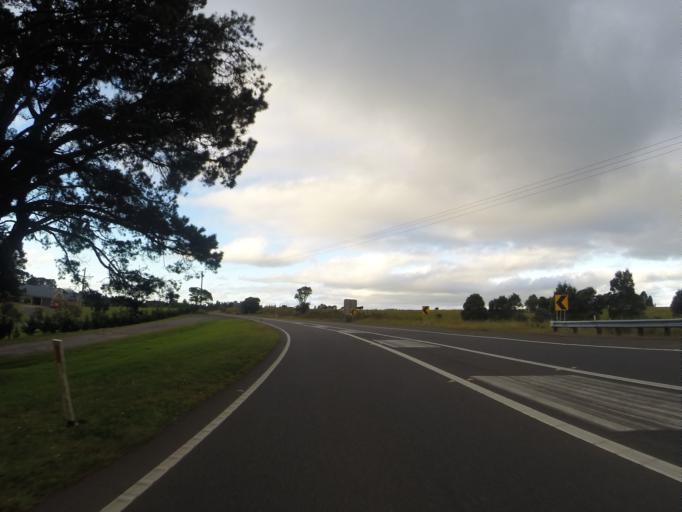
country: AU
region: New South Wales
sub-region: Shellharbour
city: Calderwood
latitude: -34.5858
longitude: 150.6269
